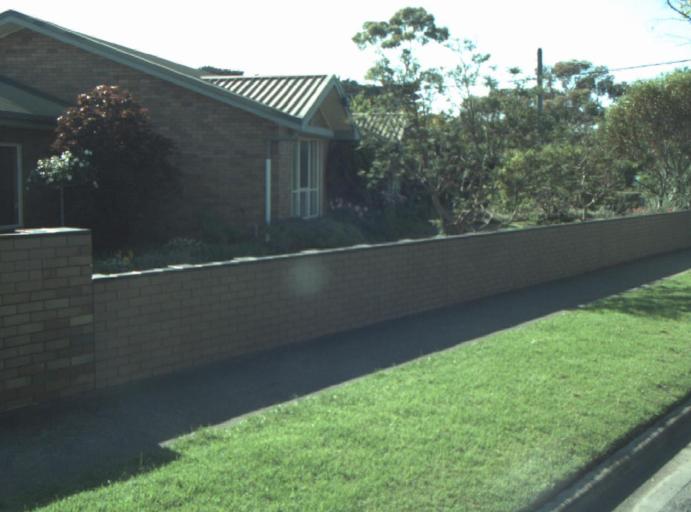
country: AU
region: Victoria
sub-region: Greater Geelong
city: Lara
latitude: -38.0204
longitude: 144.4061
